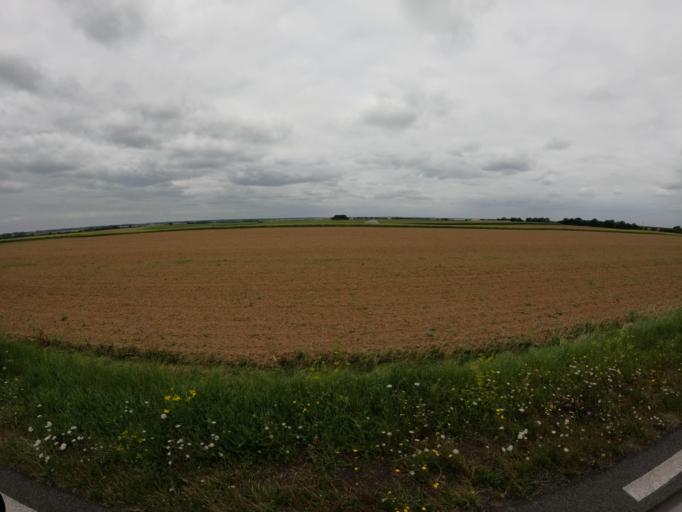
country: FR
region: Pays de la Loire
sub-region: Departement de la Vendee
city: Sainte-Hermine
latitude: 46.5417
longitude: -1.0265
